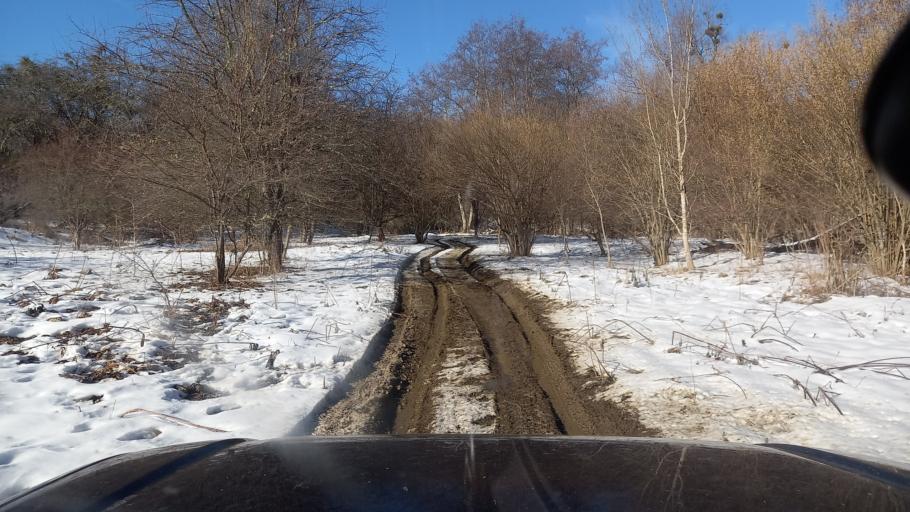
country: RU
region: Adygeya
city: Kamennomostskiy
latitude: 44.2057
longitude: 40.1482
